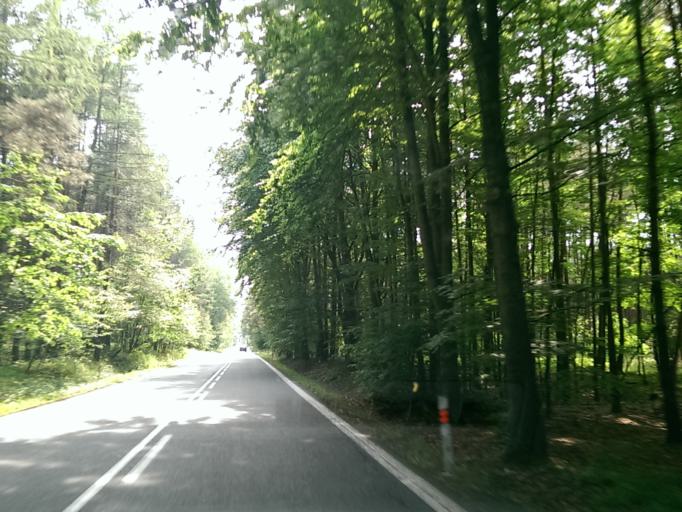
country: CZ
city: Bila Tremesna
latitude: 50.4203
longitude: 15.7137
